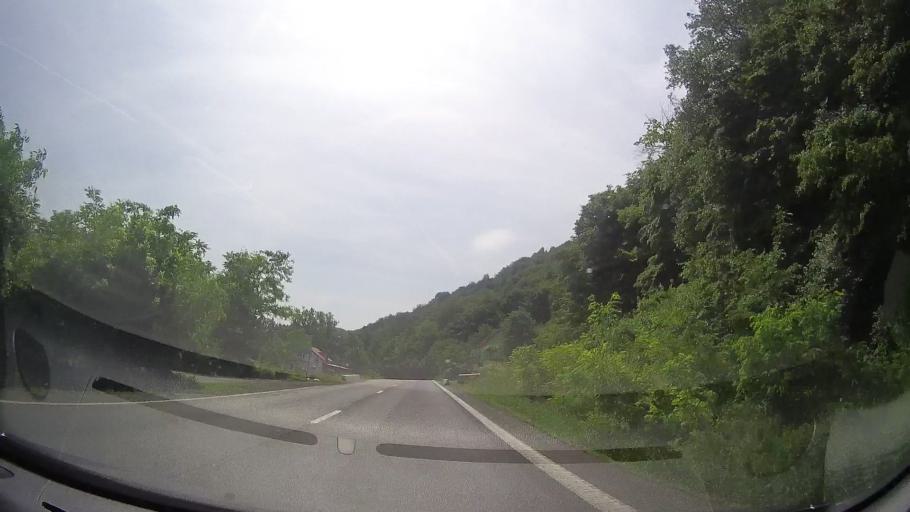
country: RO
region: Hunedoara
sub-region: Comuna Branisca
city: Branisca
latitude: 45.9109
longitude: 22.7695
